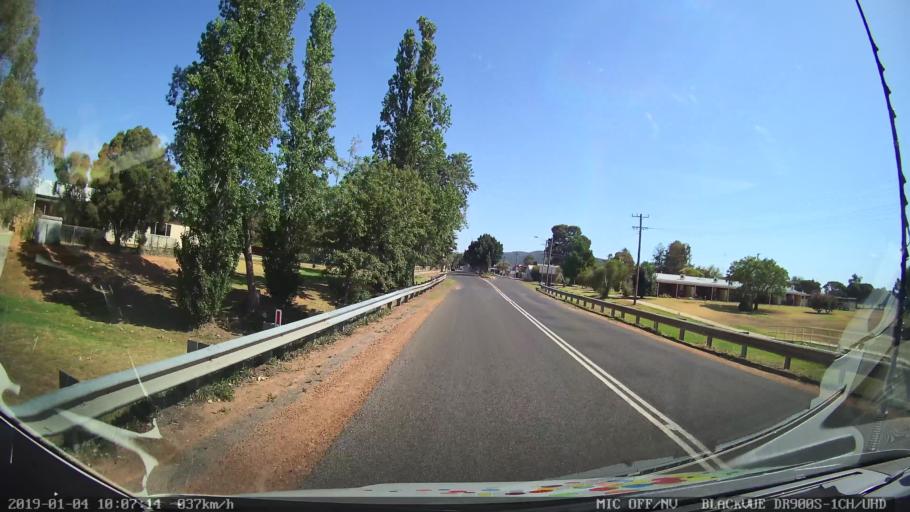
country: AU
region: New South Wales
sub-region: Cabonne
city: Canowindra
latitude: -33.4295
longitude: 148.3715
